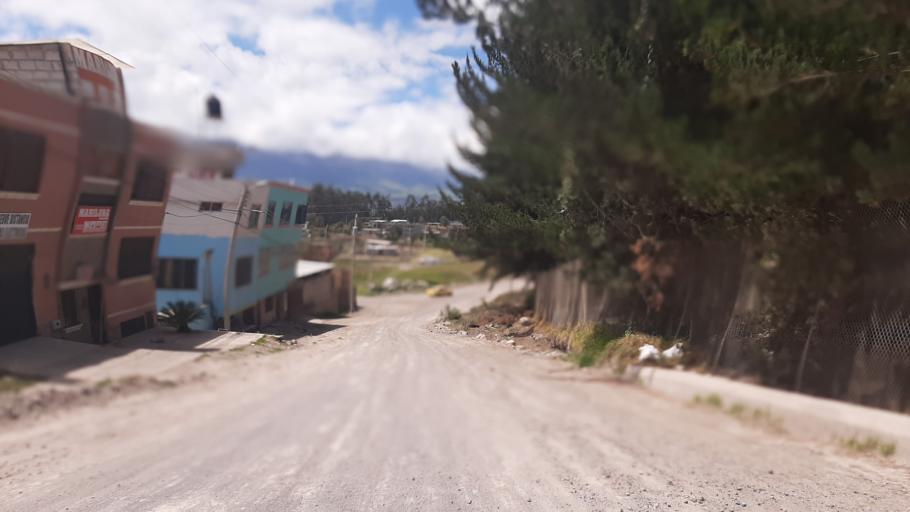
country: EC
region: Chimborazo
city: Riobamba
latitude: -1.6506
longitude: -78.6414
